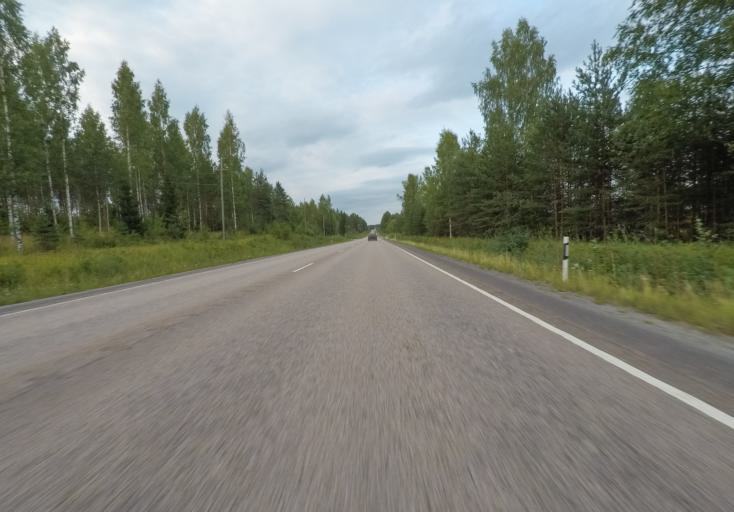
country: FI
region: Central Finland
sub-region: Joutsa
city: Joutsa
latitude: 61.7240
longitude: 26.0855
